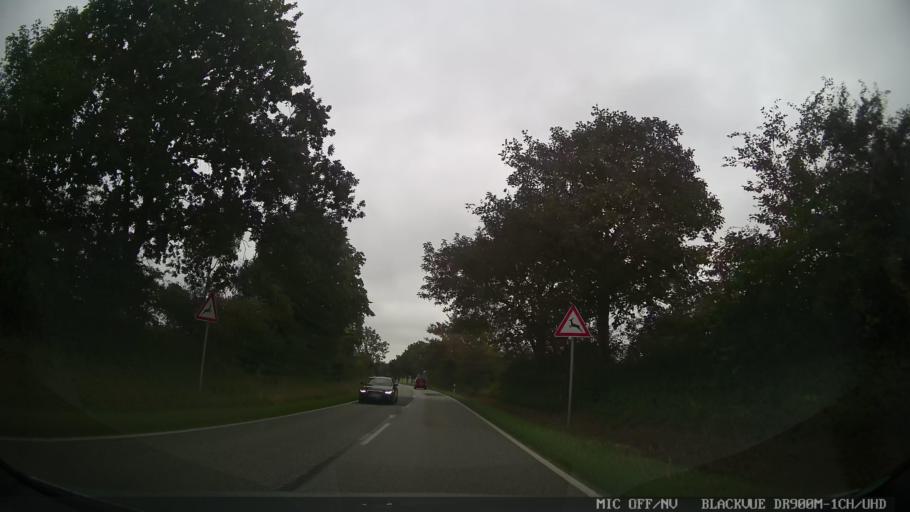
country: DE
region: Schleswig-Holstein
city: Neukirchen
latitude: 54.3096
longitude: 11.0115
